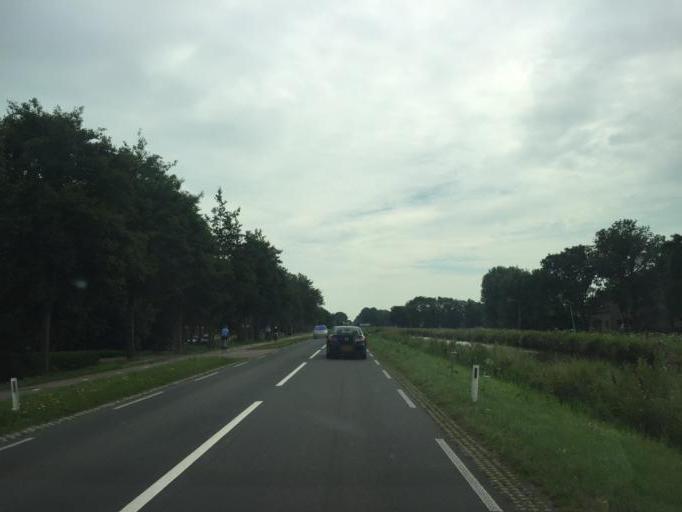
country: NL
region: North Holland
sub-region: Gemeente Alkmaar
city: Alkmaar
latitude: 52.6184
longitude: 4.7882
